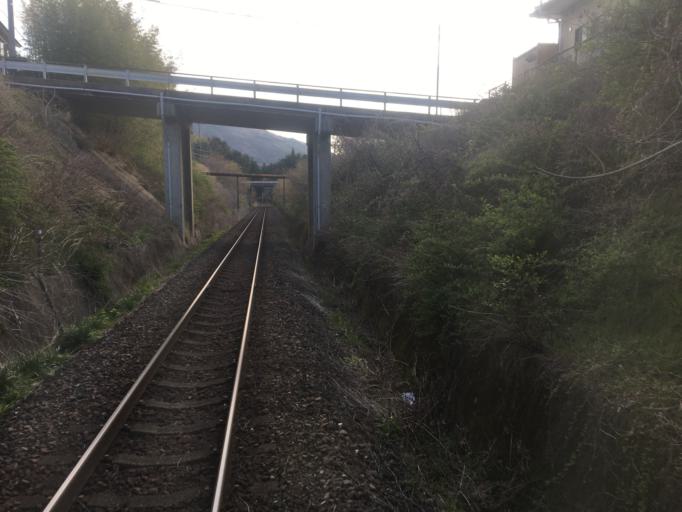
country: JP
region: Iwate
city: Kamaishi
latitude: 39.1516
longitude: 141.8374
